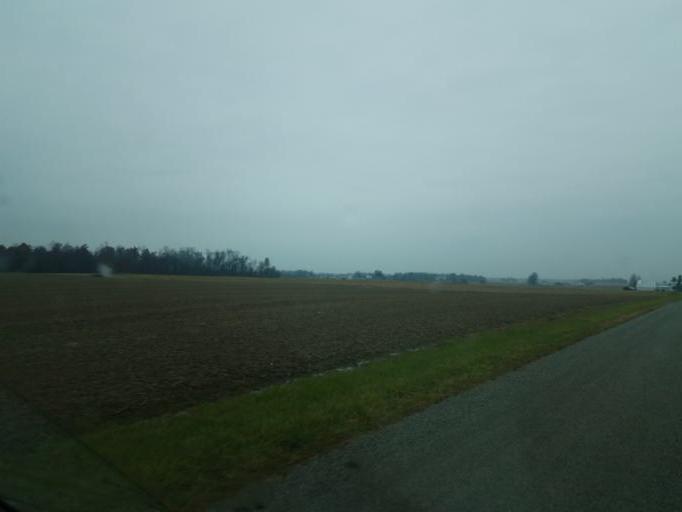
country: US
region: Ohio
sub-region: Knox County
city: Centerburg
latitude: 40.2349
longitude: -82.7233
